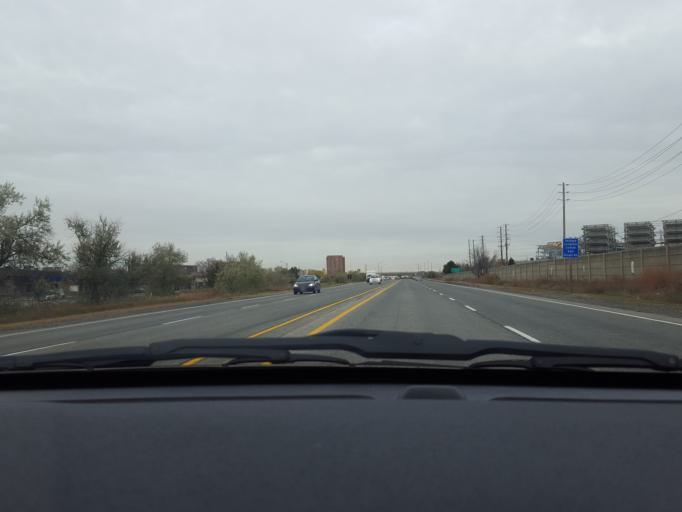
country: CA
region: Ontario
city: Etobicoke
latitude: 43.6832
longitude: -79.5800
